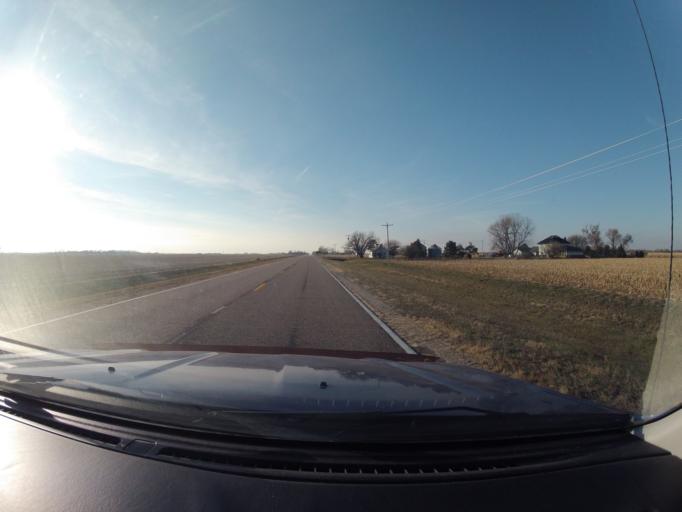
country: US
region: Nebraska
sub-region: Buffalo County
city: Kearney
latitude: 40.6410
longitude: -98.9724
